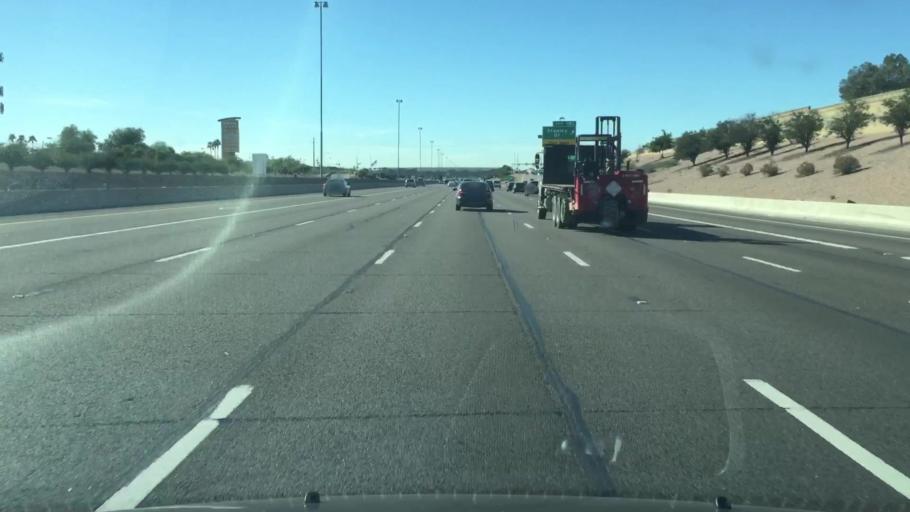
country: US
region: Arizona
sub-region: Maricopa County
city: Gilbert
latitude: 33.3854
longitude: -111.7992
